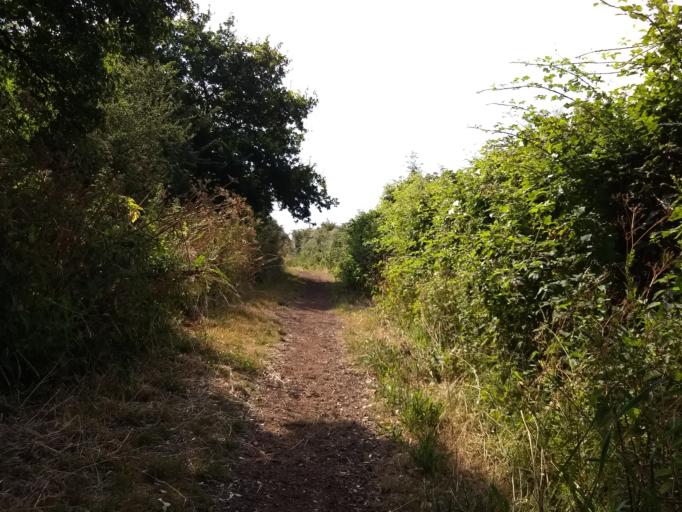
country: GB
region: England
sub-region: Isle of Wight
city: Ryde
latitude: 50.7151
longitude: -1.1587
